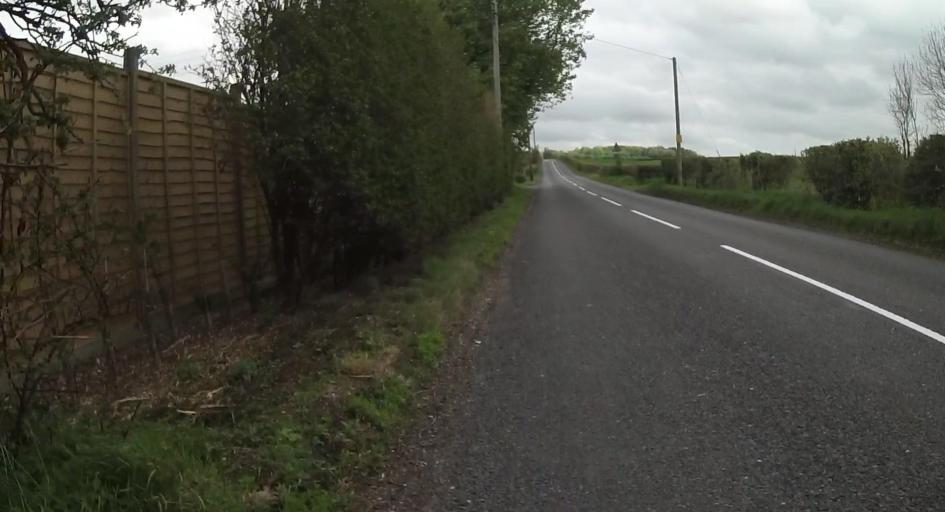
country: GB
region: England
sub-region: Hampshire
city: Colden Common
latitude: 51.0190
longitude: -1.2578
